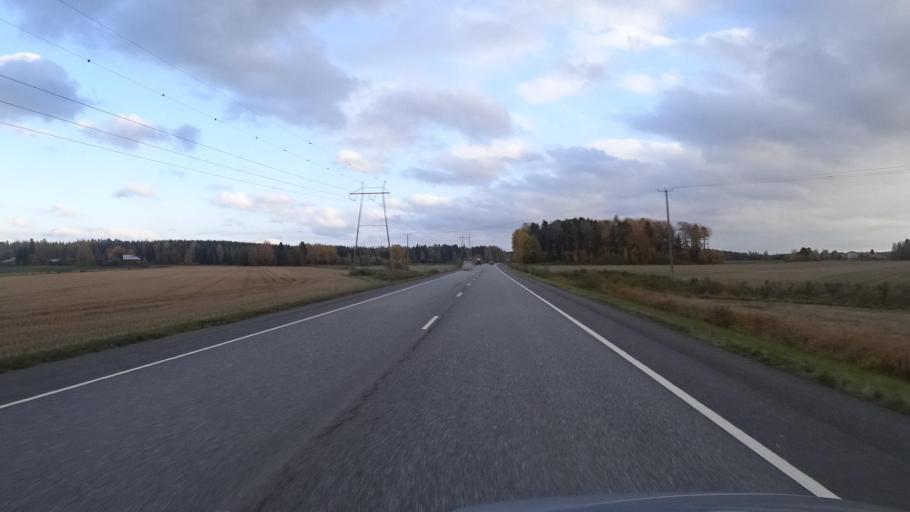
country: FI
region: Satakunta
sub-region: Rauma
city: Saekylae
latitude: 61.0277
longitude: 22.3996
